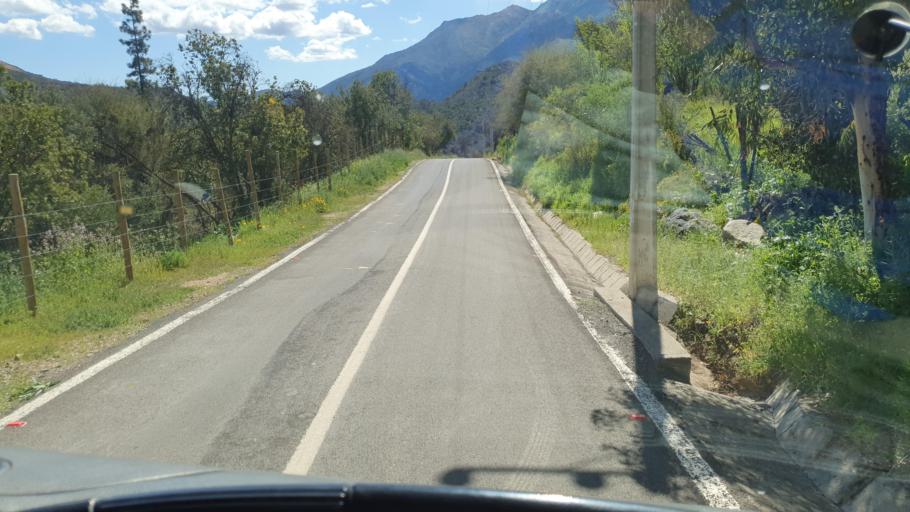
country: CL
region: Valparaiso
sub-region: Provincia de Marga Marga
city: Limache
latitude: -33.1890
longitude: -71.0999
